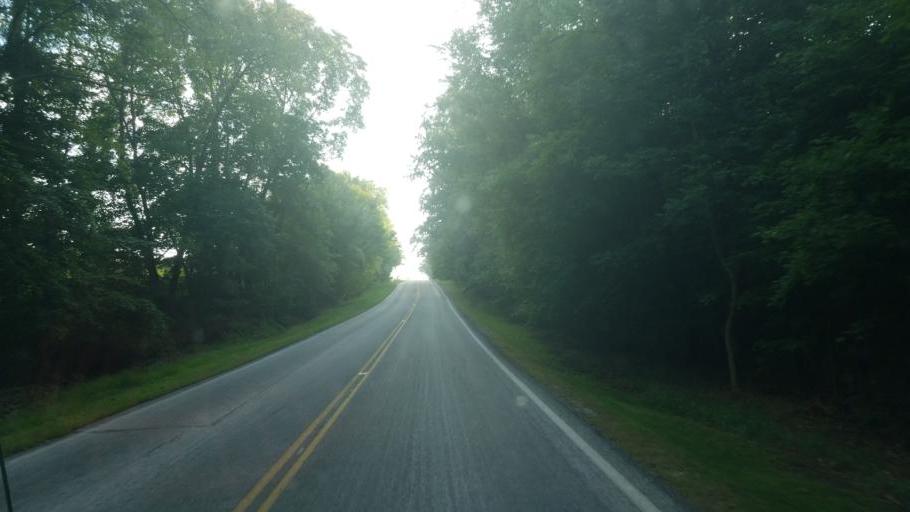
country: US
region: Ohio
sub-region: Ashland County
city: Loudonville
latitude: 40.7444
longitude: -82.1587
